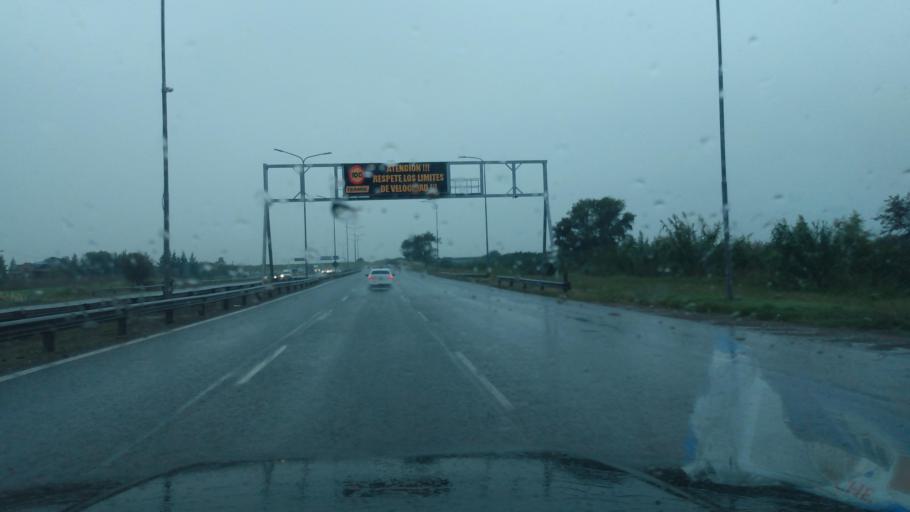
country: AR
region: Buenos Aires
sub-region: Partido de Tigre
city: Tigre
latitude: -34.4916
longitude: -58.5959
